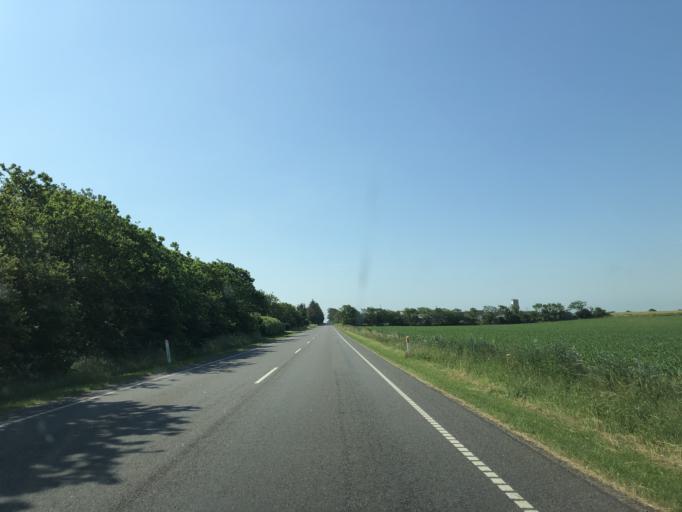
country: DK
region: South Denmark
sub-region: Varde Kommune
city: Varde
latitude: 55.6681
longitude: 8.4906
